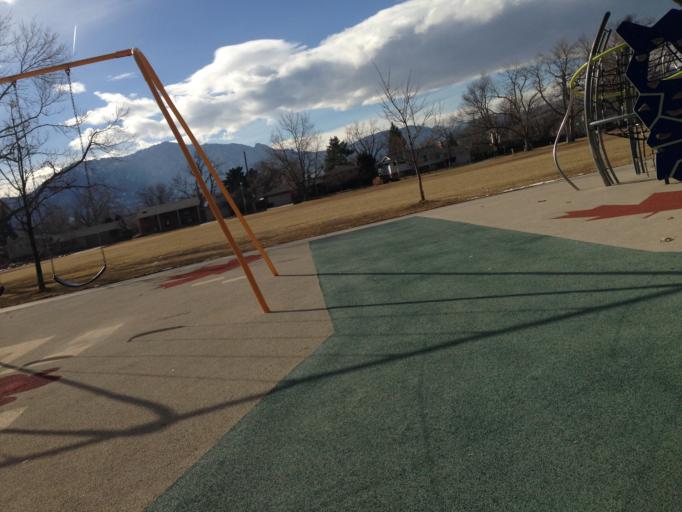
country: US
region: Colorado
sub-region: Boulder County
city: Boulder
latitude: 39.9927
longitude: -105.2276
